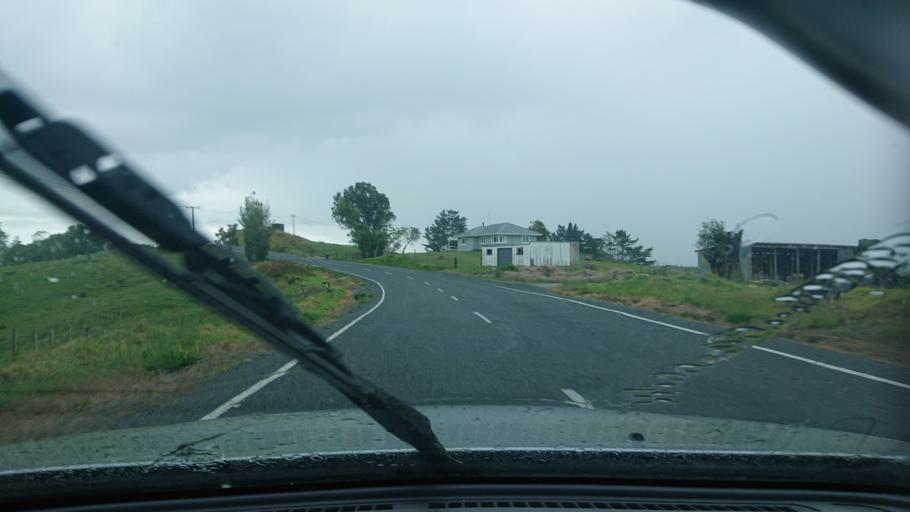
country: NZ
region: Auckland
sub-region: Auckland
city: Wellsford
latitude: -36.3280
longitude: 174.4105
